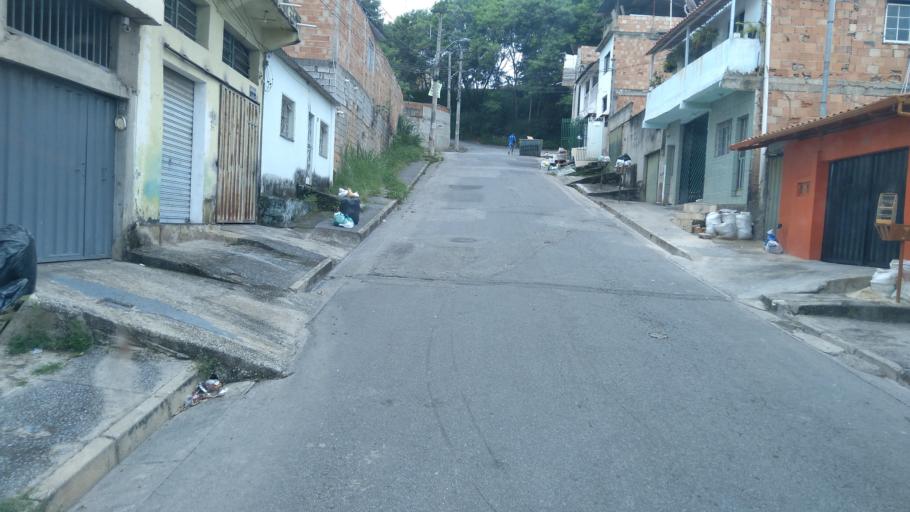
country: BR
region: Minas Gerais
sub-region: Belo Horizonte
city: Belo Horizonte
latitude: -19.8477
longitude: -43.9097
